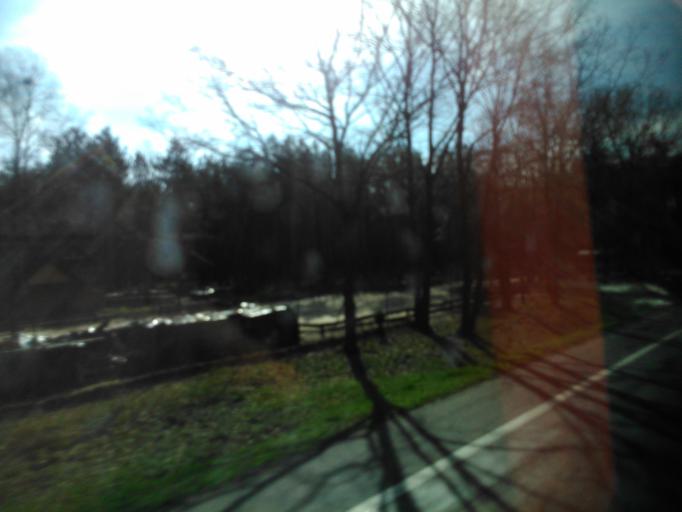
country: PL
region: Kujawsko-Pomorskie
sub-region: Powiat aleksandrowski
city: Aleksandrow Kujawski
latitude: 52.8921
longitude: 18.7310
